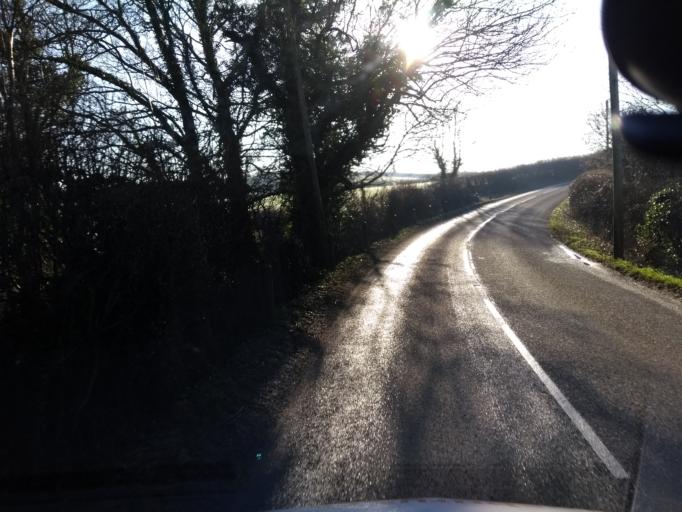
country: GB
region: England
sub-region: Somerset
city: Redlynch
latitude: 51.0903
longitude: -2.4151
